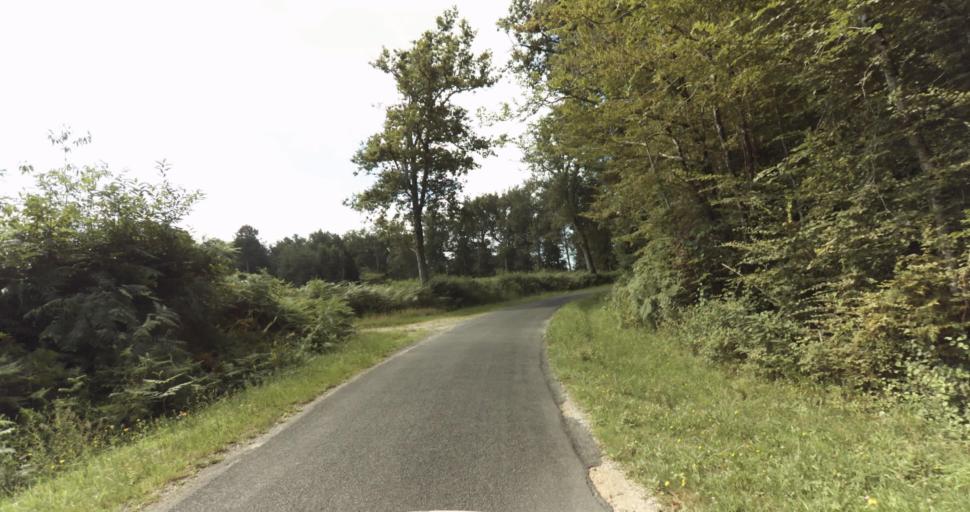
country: FR
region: Aquitaine
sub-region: Departement de la Gironde
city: Bazas
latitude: 44.4590
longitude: -0.2165
